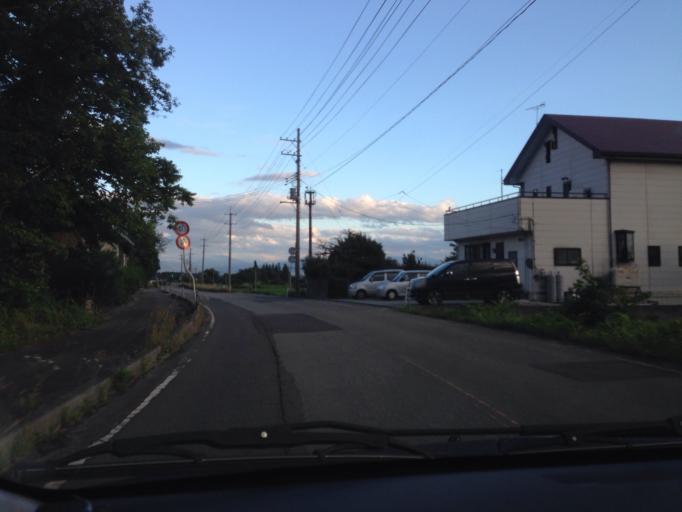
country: JP
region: Fukushima
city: Kitakata
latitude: 37.6894
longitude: 139.8578
